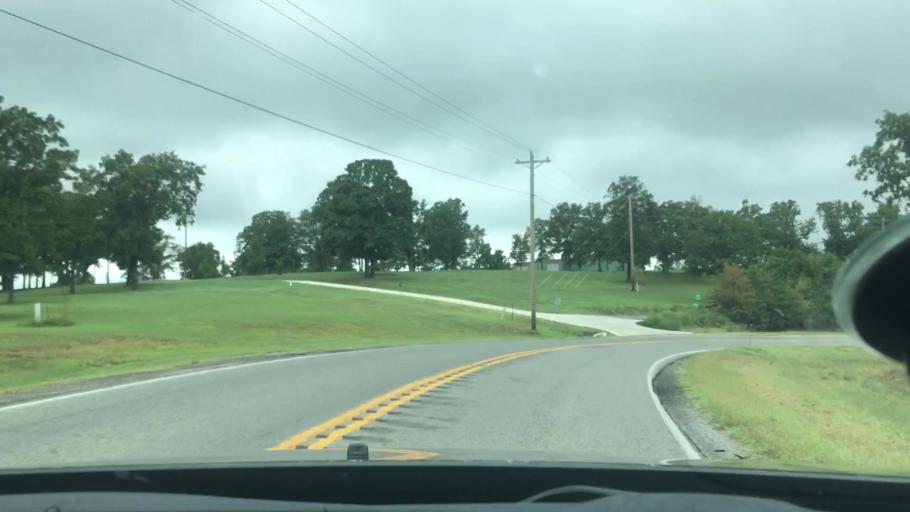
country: US
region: Oklahoma
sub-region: Sequoyah County
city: Vian
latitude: 35.6274
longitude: -94.9647
